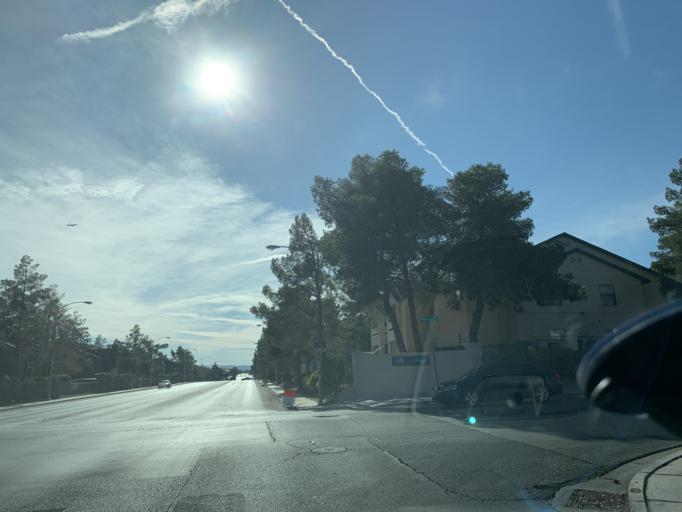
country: US
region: Nevada
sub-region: Clark County
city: Spring Valley
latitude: 36.0968
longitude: -115.2167
